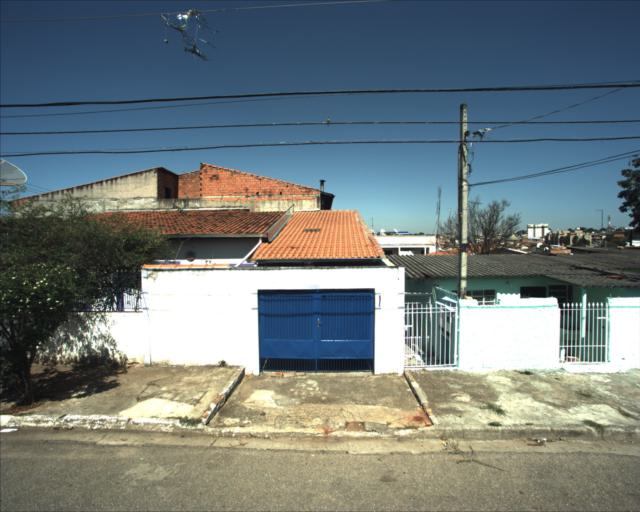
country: BR
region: Sao Paulo
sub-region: Sorocaba
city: Sorocaba
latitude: -23.4759
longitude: -47.4785
